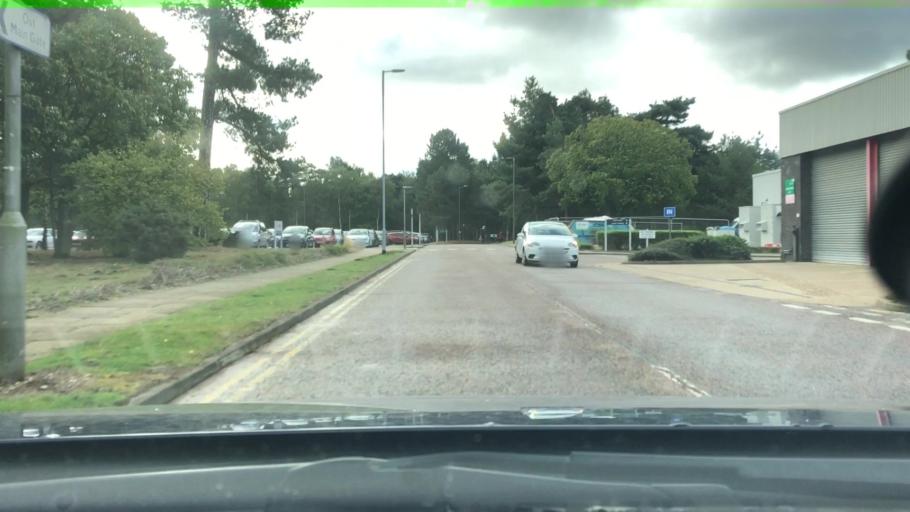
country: GB
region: England
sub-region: Suffolk
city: Kesgrave
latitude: 52.0568
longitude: 1.2831
